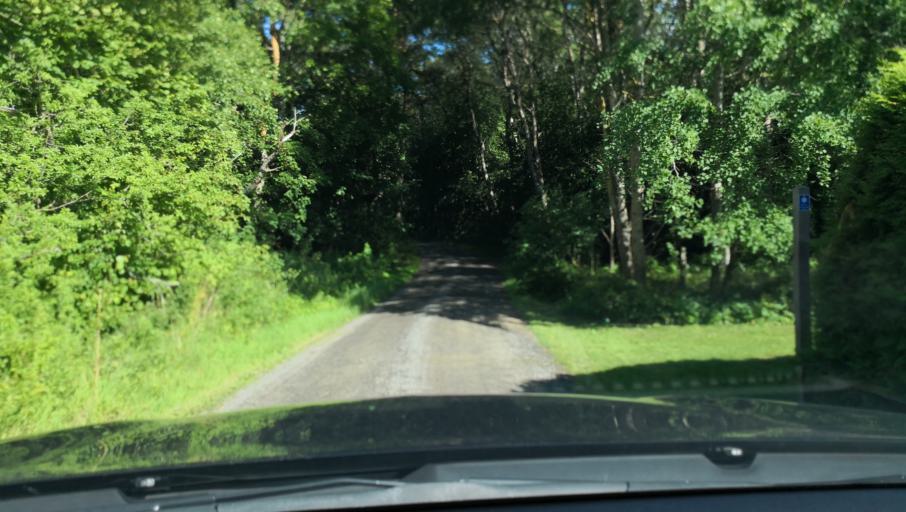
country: SE
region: Skane
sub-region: Kristianstads Kommun
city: Degeberga
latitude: 55.8079
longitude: 14.1962
